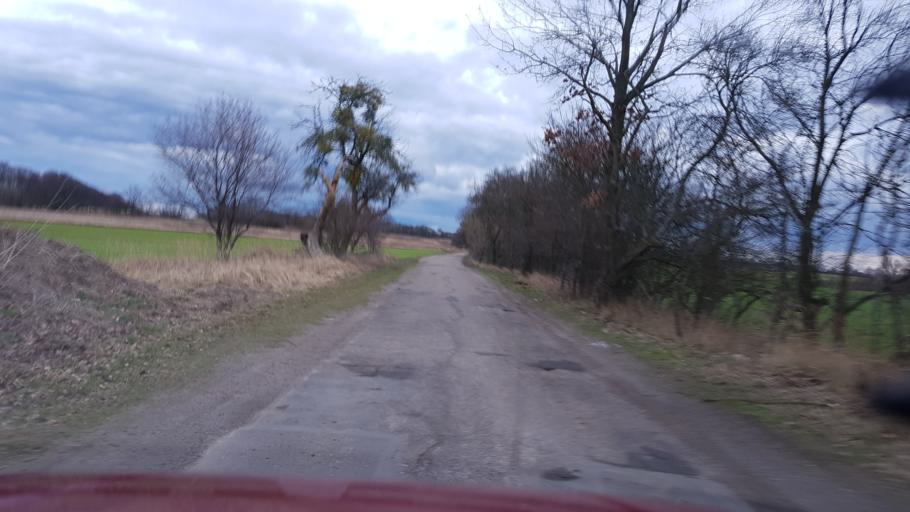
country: PL
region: West Pomeranian Voivodeship
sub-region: Powiat gryfinski
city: Stare Czarnowo
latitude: 53.3309
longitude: 14.6702
